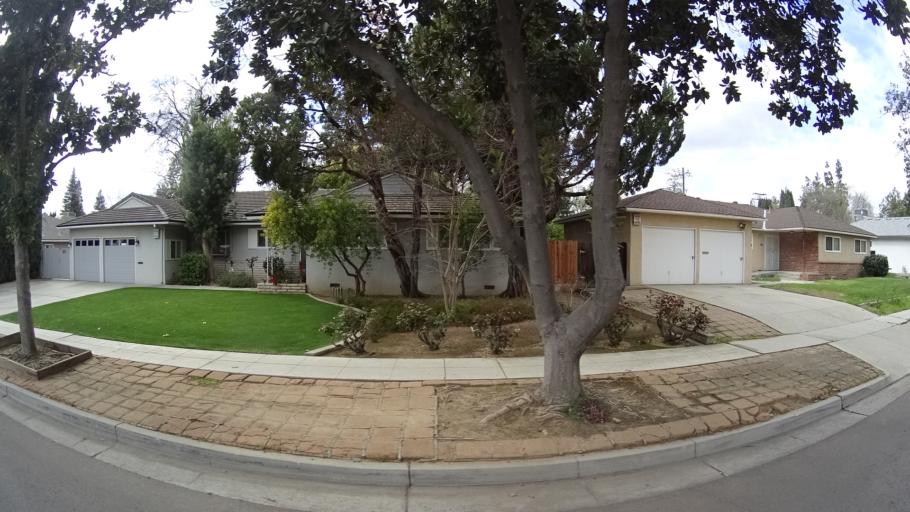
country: US
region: California
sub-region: Fresno County
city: Clovis
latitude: 36.8224
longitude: -119.7672
